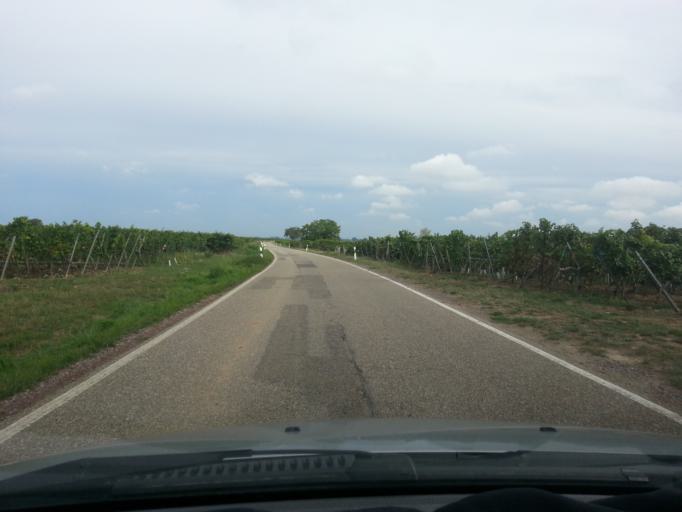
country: DE
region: Rheinland-Pfalz
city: Kirrweiler
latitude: 49.3032
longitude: 8.1687
